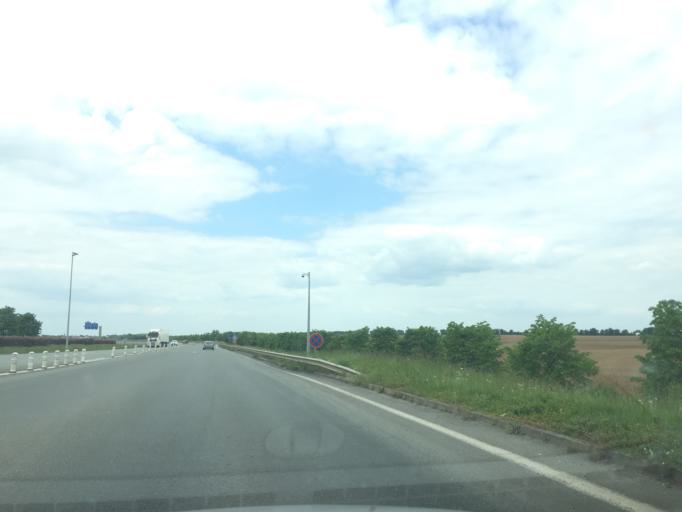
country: FR
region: Poitou-Charentes
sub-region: Departement des Deux-Sevres
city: La Creche
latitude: 46.3555
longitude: -0.3313
